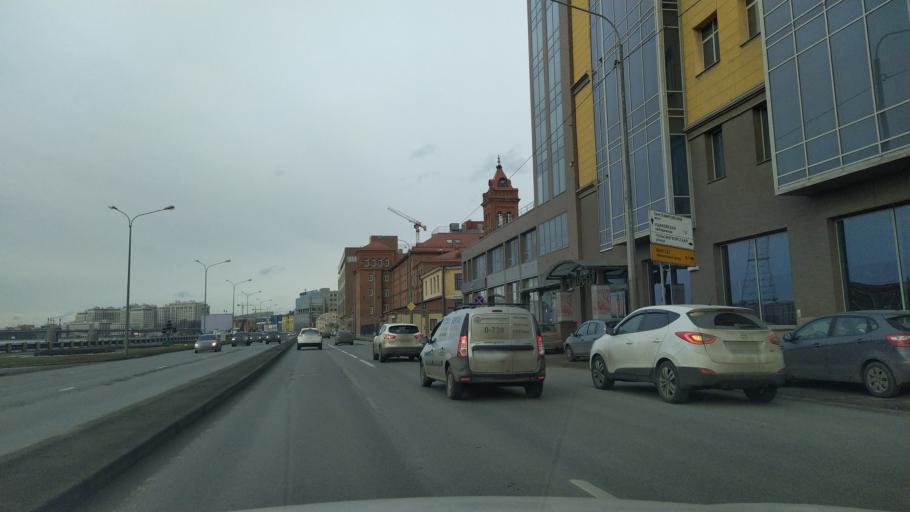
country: RU
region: Leningrad
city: Sampsonievskiy
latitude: 59.9733
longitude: 30.3337
